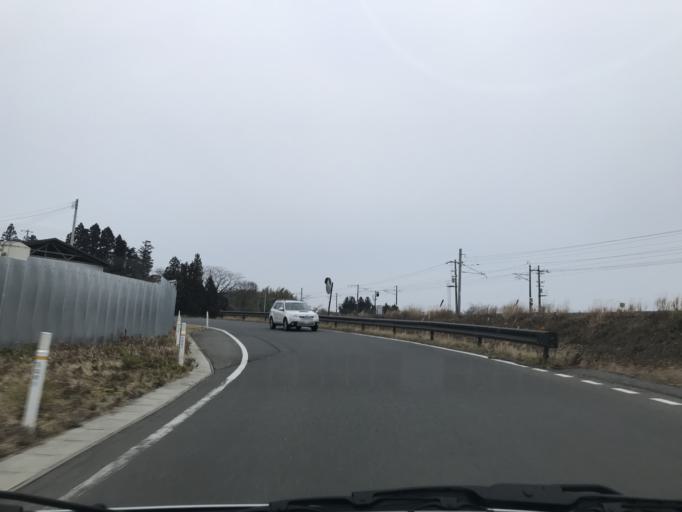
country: JP
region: Miyagi
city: Kogota
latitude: 38.6882
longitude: 141.0951
